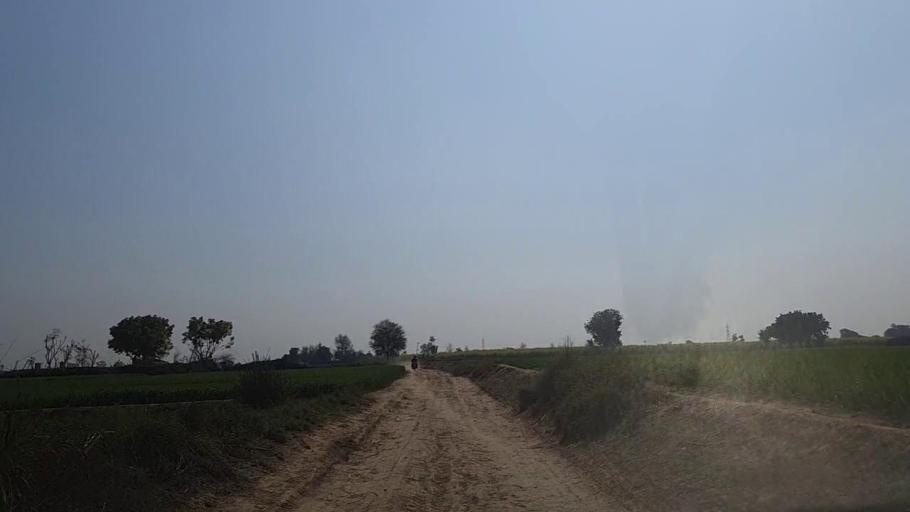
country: PK
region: Sindh
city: Moro
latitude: 26.6974
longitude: 67.9276
